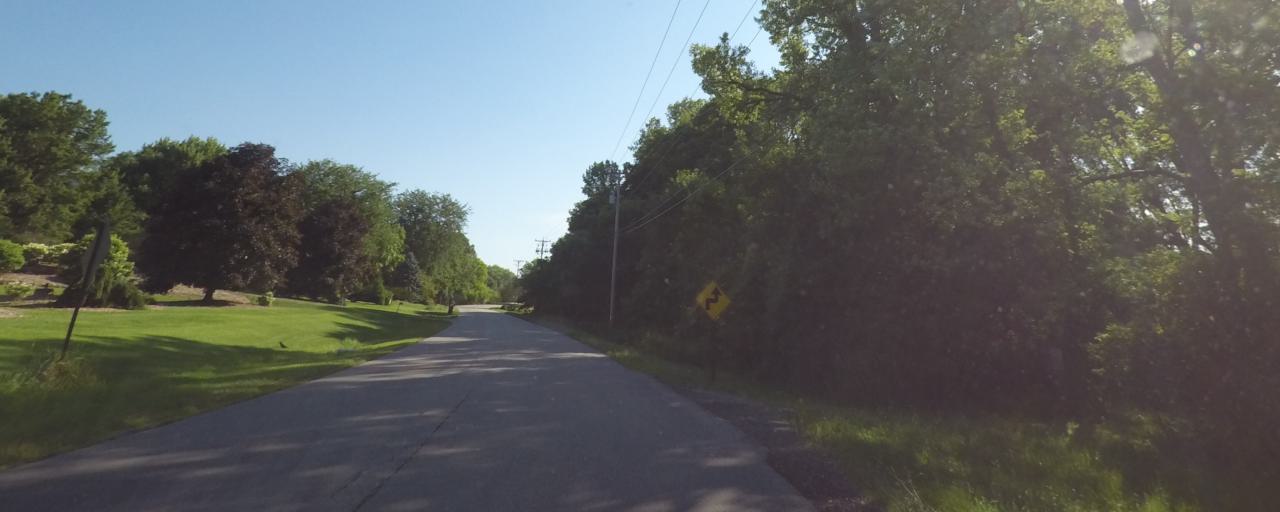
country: US
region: Wisconsin
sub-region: Dane County
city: McFarland
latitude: 43.0026
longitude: -89.3046
